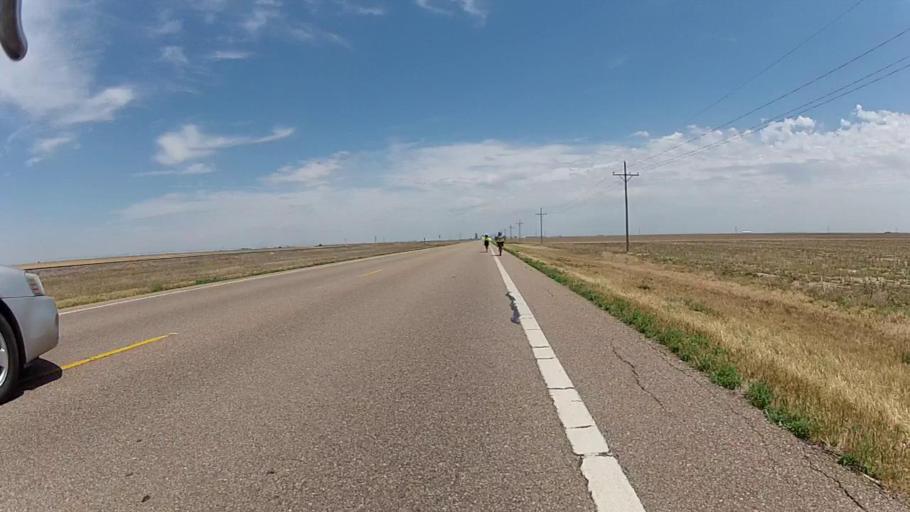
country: US
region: Kansas
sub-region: Haskell County
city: Sublette
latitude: 37.4652
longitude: -100.9085
